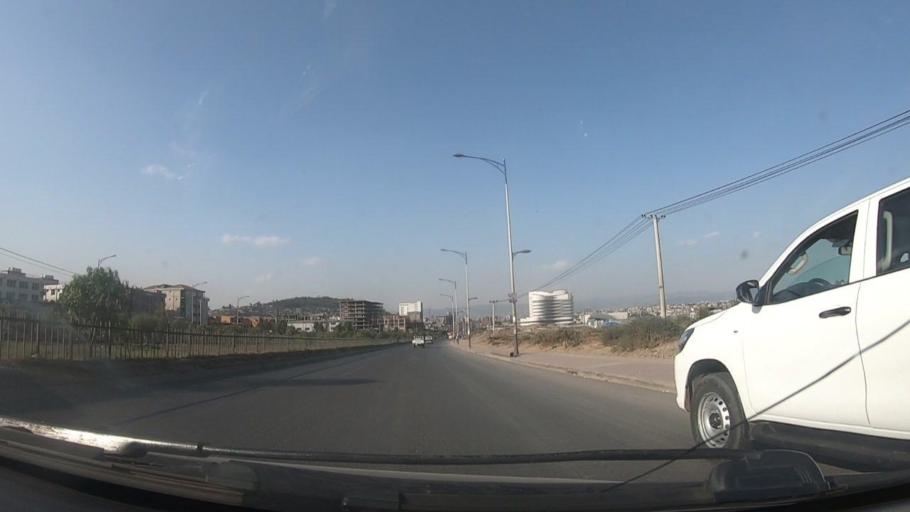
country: ET
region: Adis Abeba
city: Addis Ababa
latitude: 8.9290
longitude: 38.7341
